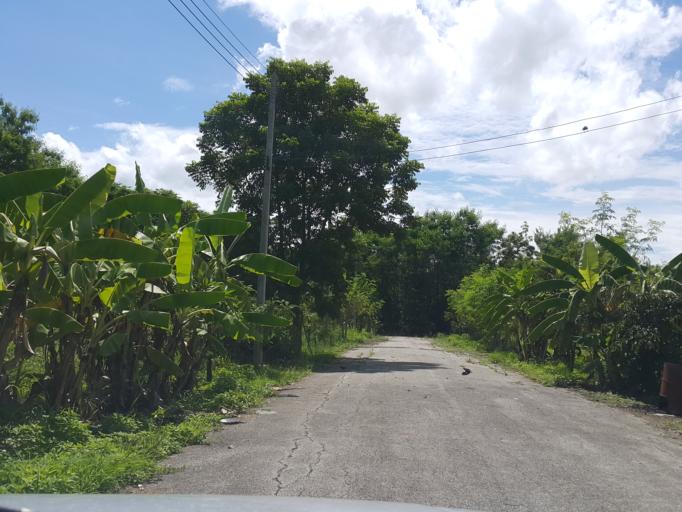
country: TH
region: Chiang Mai
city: San Kamphaeng
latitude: 18.7642
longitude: 99.1188
